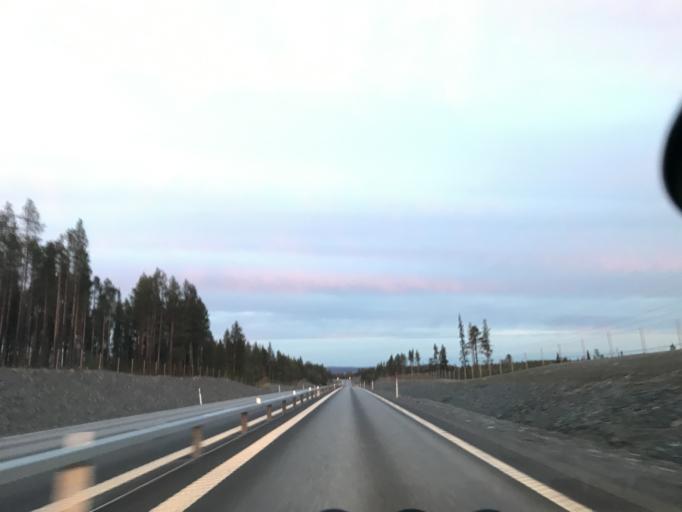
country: SE
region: Norrbotten
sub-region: Gallivare Kommun
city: Malmberget
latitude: 67.6821
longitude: 20.8708
